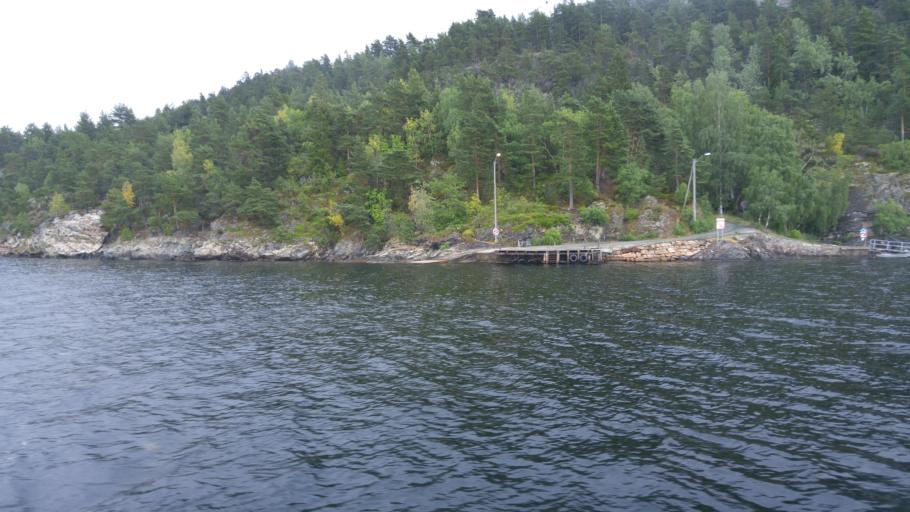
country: NO
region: Akershus
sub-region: Nesodden
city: Nesoddtangen
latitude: 59.8185
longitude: 10.6166
